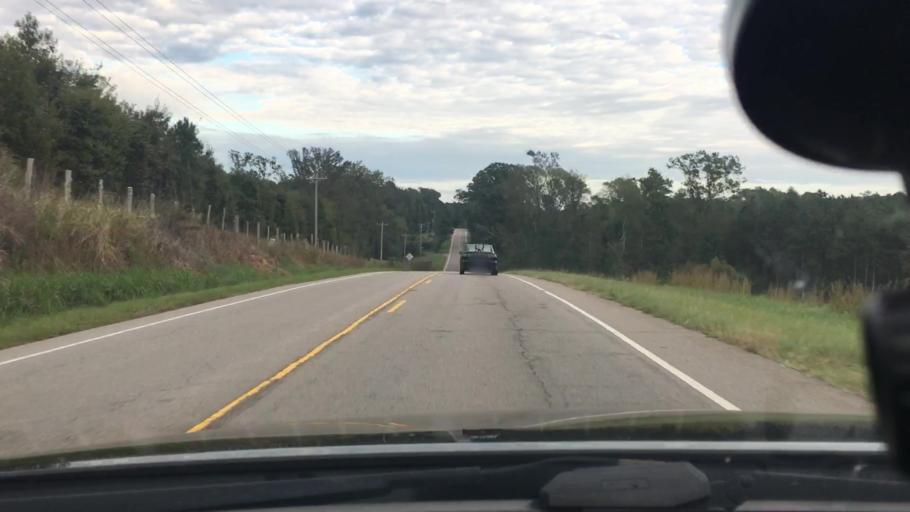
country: US
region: North Carolina
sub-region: Moore County
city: Robbins
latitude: 35.3986
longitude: -79.5465
